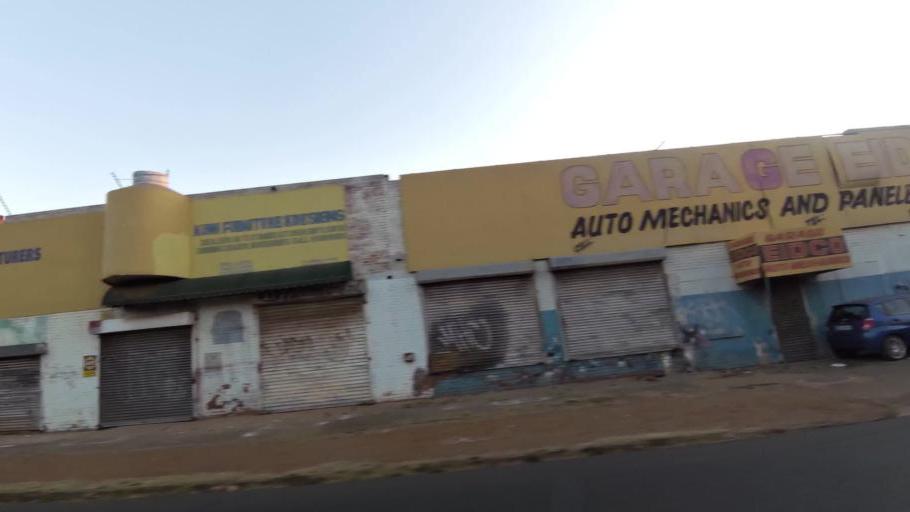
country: ZA
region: Gauteng
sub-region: City of Johannesburg Metropolitan Municipality
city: Johannesburg
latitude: -26.2002
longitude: 27.9800
